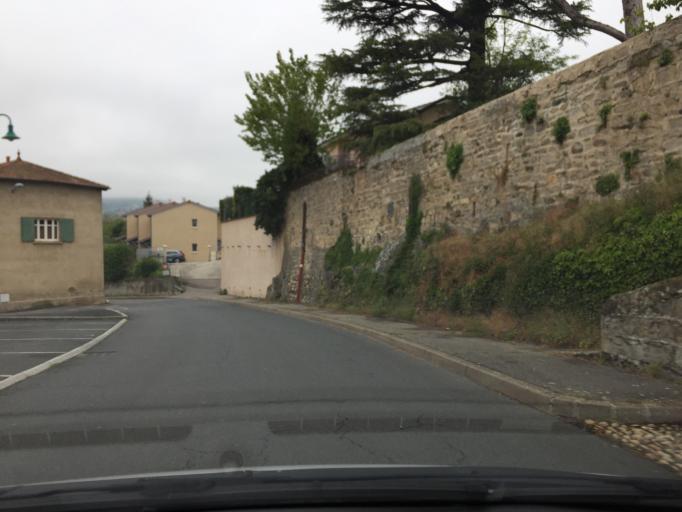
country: FR
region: Rhone-Alpes
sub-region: Departement du Rhone
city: Mornant
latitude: 45.6199
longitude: 4.6684
